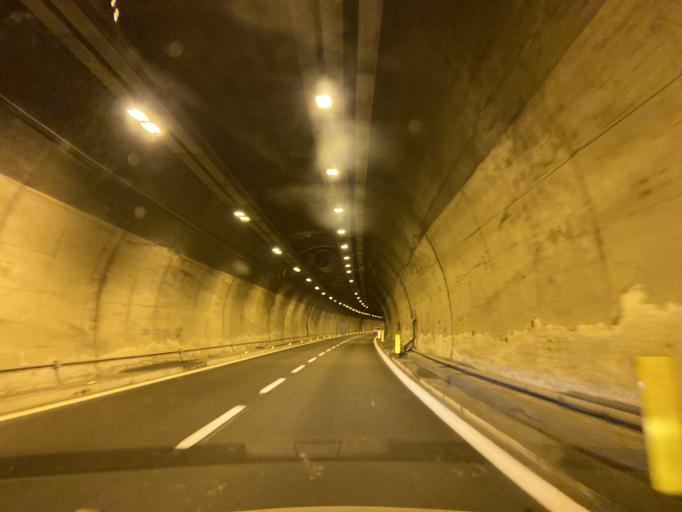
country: IT
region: Piedmont
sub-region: Provincia di Torino
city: Salbertrand
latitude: 45.0804
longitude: 6.8963
